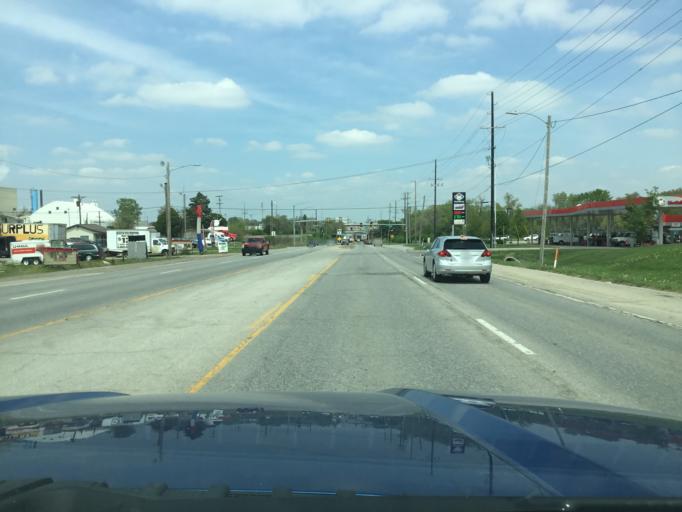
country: US
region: Kansas
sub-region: Shawnee County
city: Topeka
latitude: 38.9838
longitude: -95.6877
